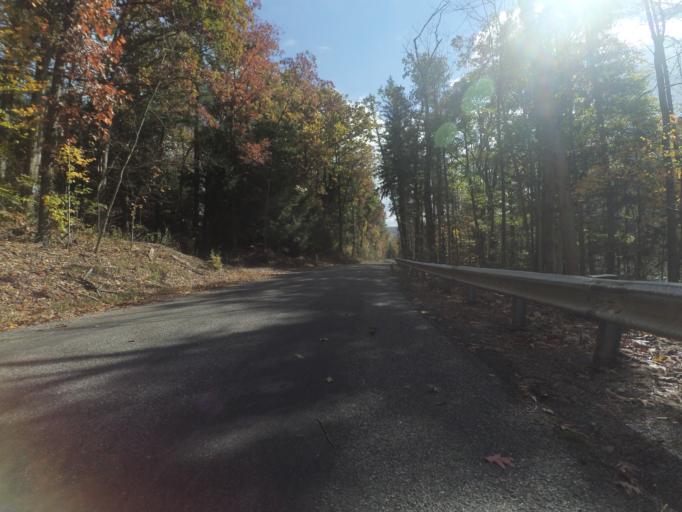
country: US
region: Pennsylvania
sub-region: Centre County
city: Park Forest Village
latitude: 40.9063
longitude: -77.9110
